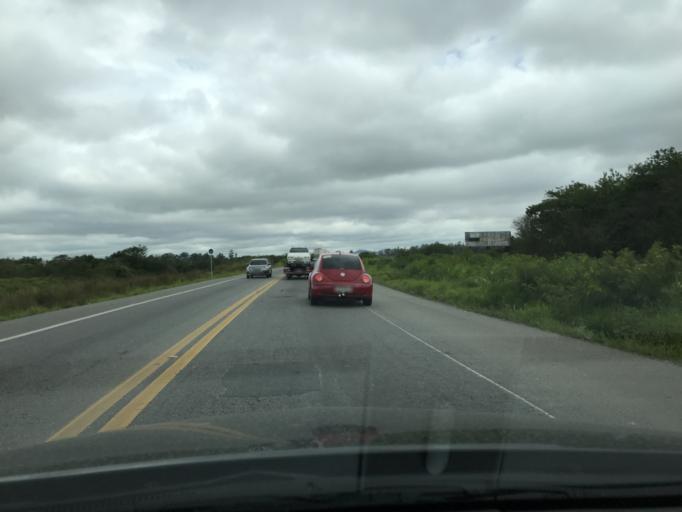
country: BR
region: Sao Paulo
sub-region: Itaquaquecetuba
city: Itaquaquecetuba
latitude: -23.4798
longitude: -46.3261
